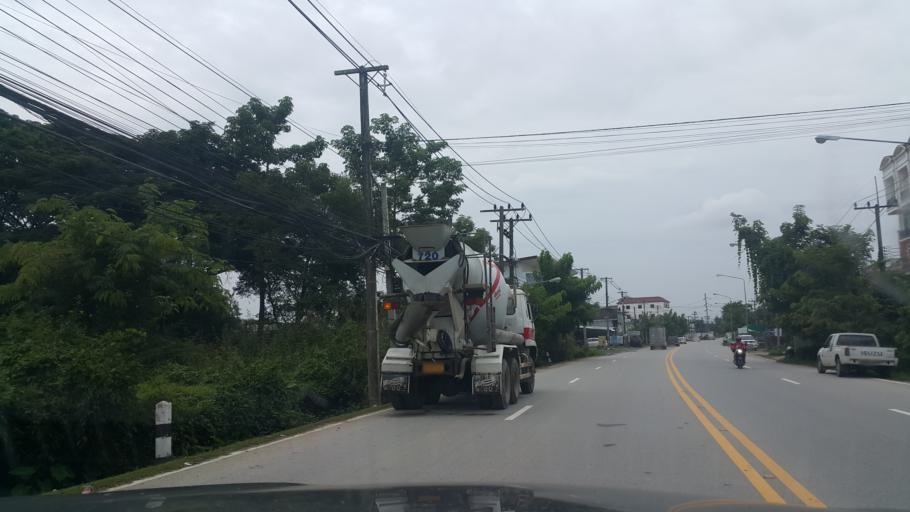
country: TH
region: Chiang Mai
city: San Sai
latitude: 18.8355
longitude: 99.0423
